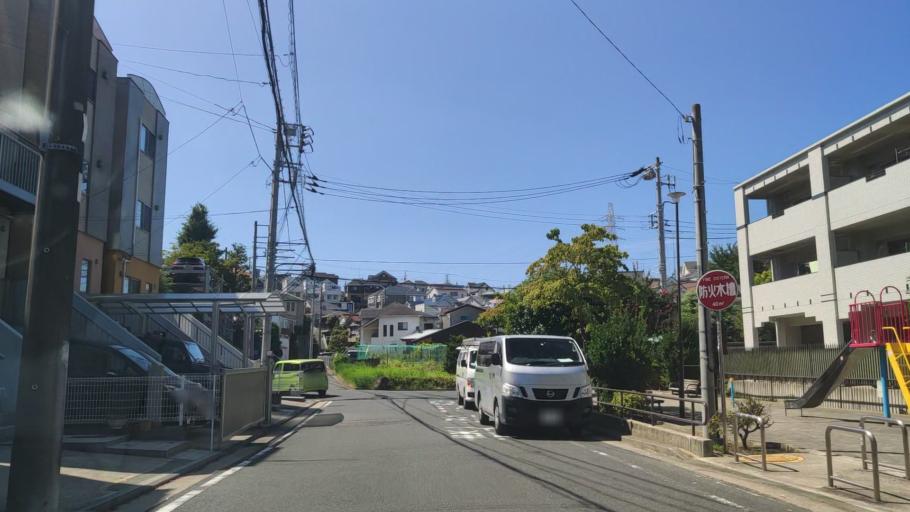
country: JP
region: Kanagawa
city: Yokohama
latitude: 35.5145
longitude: 139.6376
